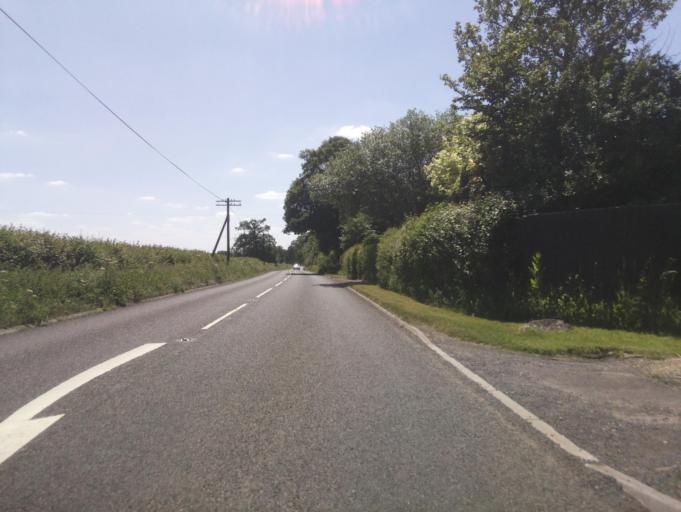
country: GB
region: England
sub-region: Wiltshire
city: Calne
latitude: 51.4673
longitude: -1.9832
